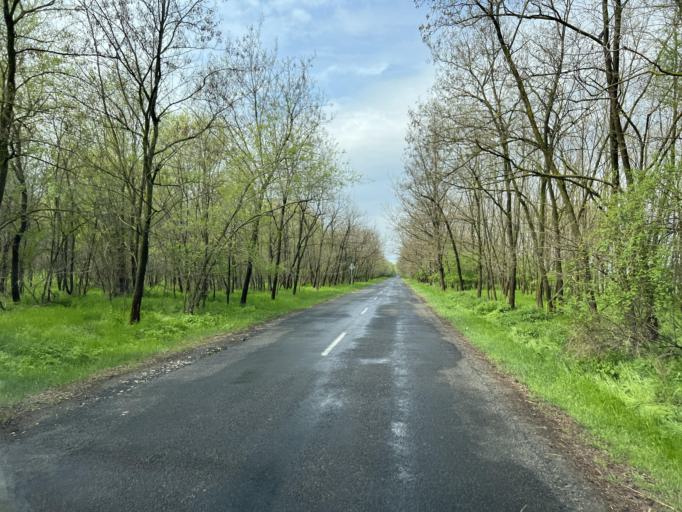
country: HU
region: Pest
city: Danszentmiklos
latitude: 47.1728
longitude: 19.5232
